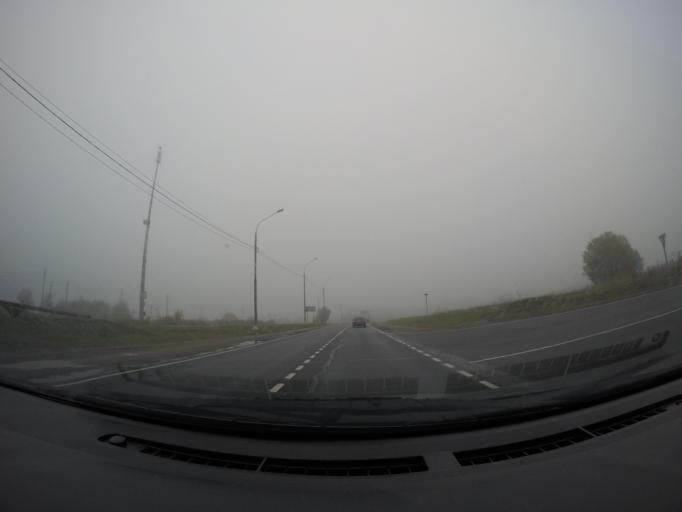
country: RU
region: Moskovskaya
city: Ruza
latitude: 55.7696
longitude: 36.2639
